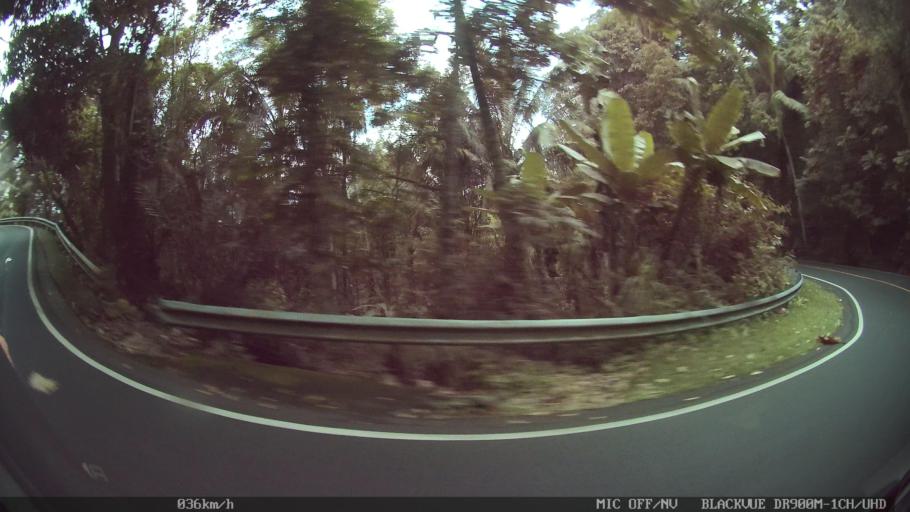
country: ID
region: Bali
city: Banjar Wangsian
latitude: -8.4809
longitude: 115.4002
